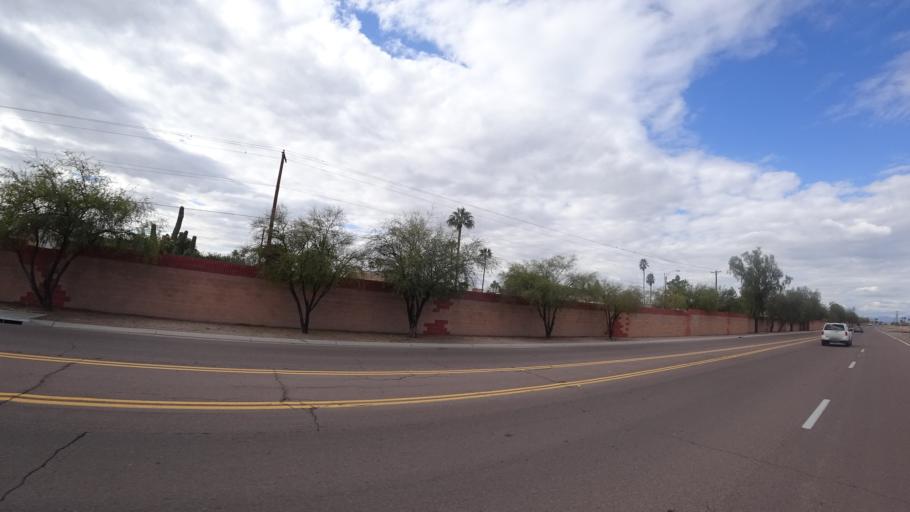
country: US
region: Arizona
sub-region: Maricopa County
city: Scottsdale
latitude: 33.5265
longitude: -111.8914
